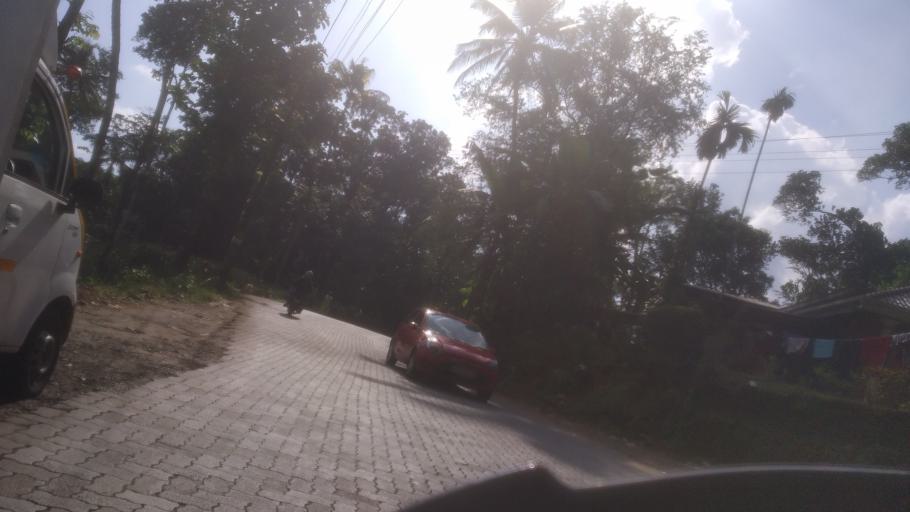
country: IN
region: Kerala
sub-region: Ernakulam
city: Muvattupula
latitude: 9.9996
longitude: 76.6348
